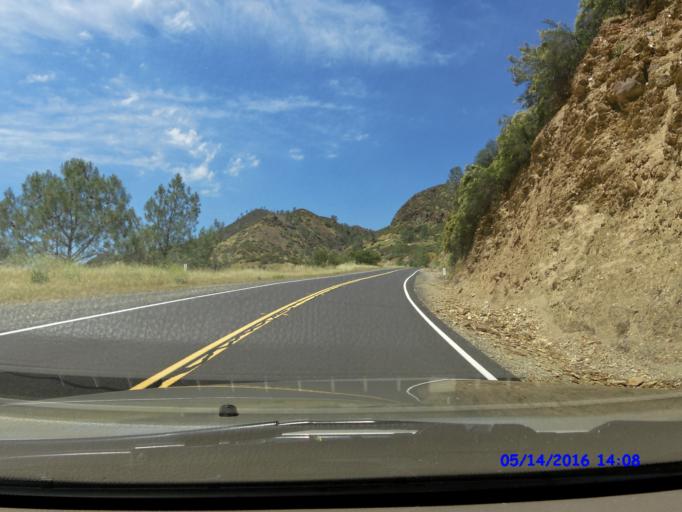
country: US
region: California
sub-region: Mariposa County
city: Mariposa
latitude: 37.6165
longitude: -120.1412
